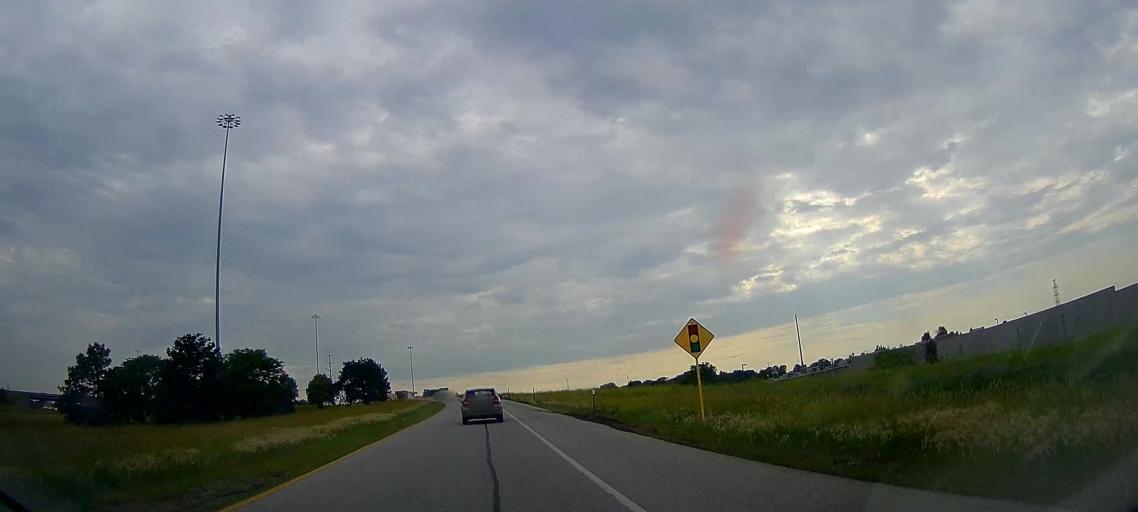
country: US
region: Nebraska
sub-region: Douglas County
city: Bennington
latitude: 41.3248
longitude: -96.0674
